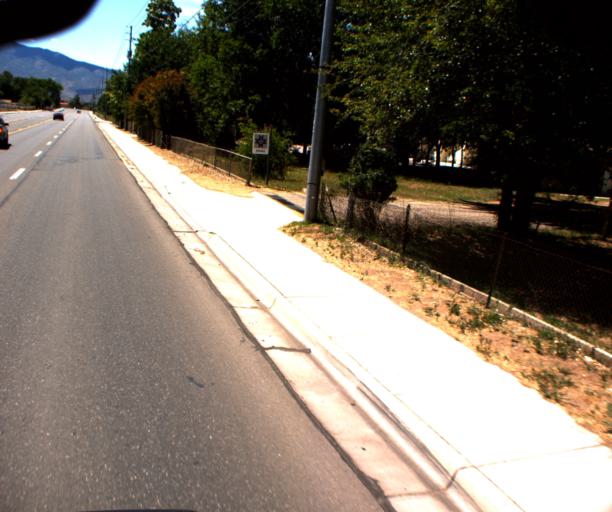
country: US
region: Arizona
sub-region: Yavapai County
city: Verde Village
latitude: 34.7213
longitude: -111.9950
